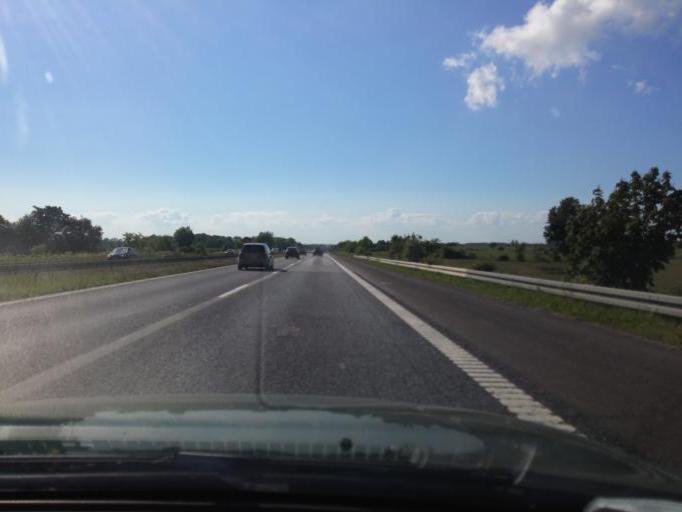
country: DK
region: South Denmark
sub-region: Assens Kommune
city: Arup
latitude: 55.4212
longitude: 10.0180
